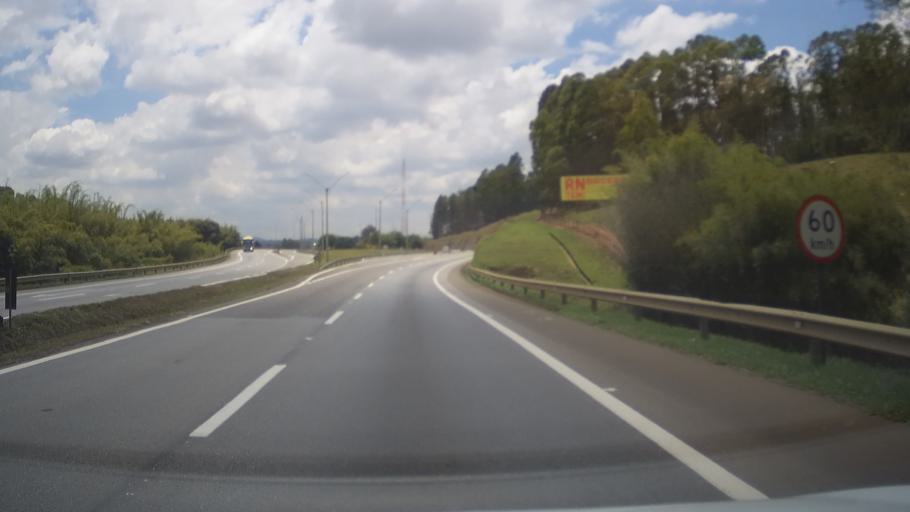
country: BR
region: Minas Gerais
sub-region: Tres Coracoes
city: Tres Coracoes
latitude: -21.6926
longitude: -45.3516
